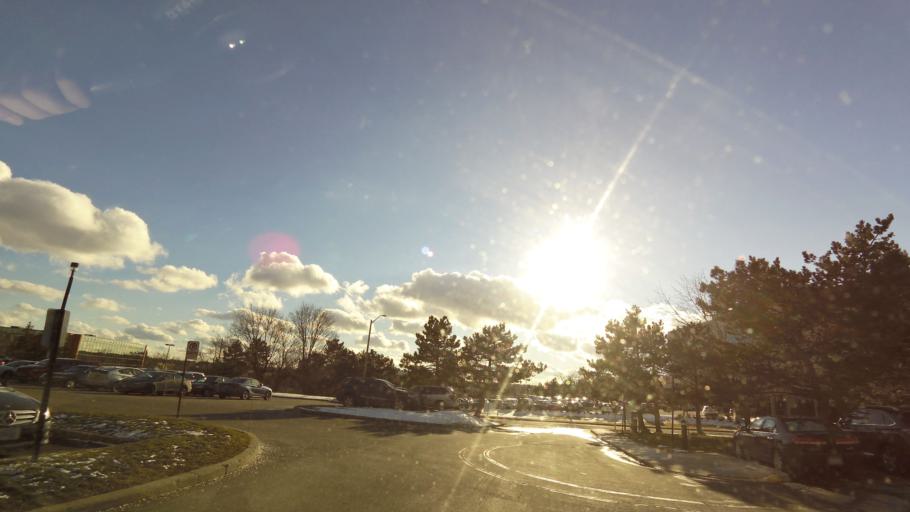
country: CA
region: Ontario
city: Brampton
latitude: 43.6011
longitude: -79.7435
